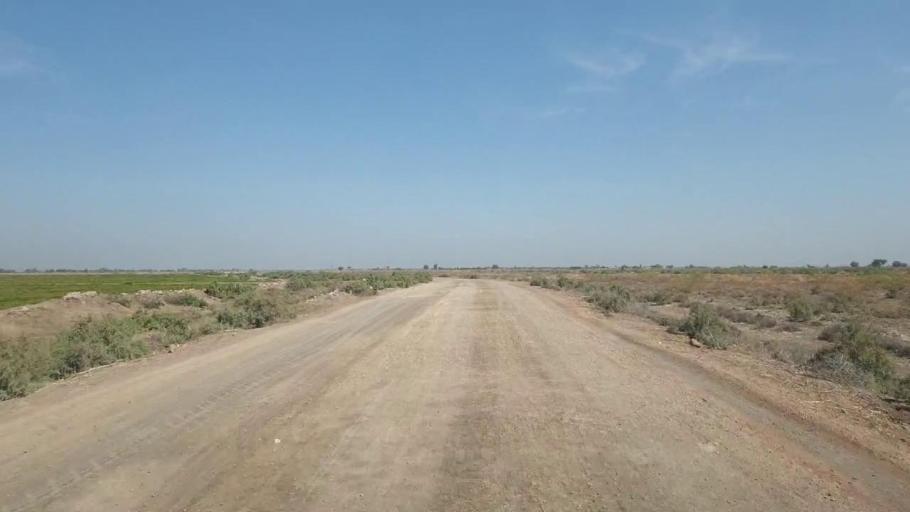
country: PK
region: Sindh
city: Samaro
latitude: 25.3538
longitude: 69.2534
